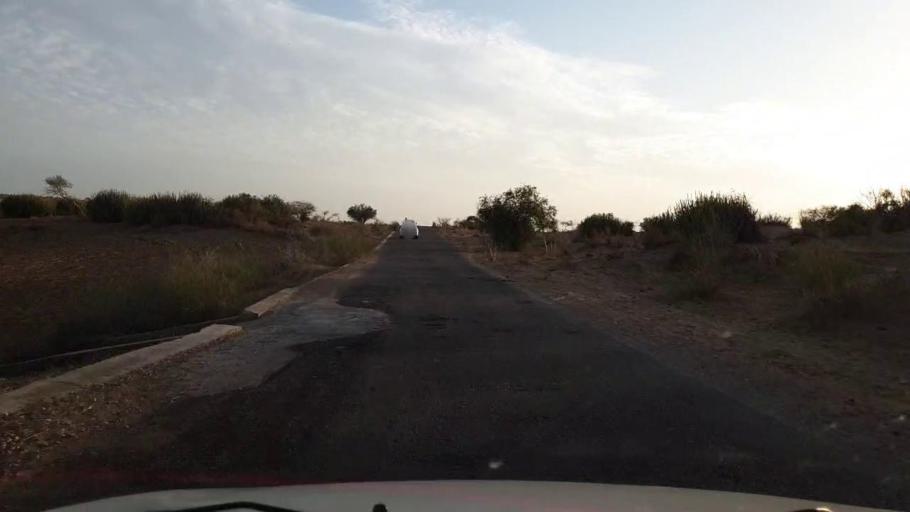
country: PK
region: Sindh
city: Nabisar
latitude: 25.0136
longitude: 69.9375
